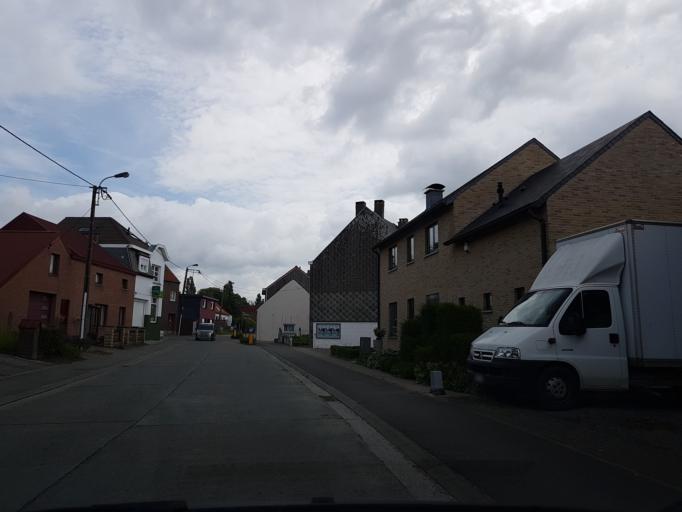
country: BE
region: Flanders
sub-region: Provincie Vlaams-Brabant
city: Ternat
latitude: 50.8931
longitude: 4.1326
